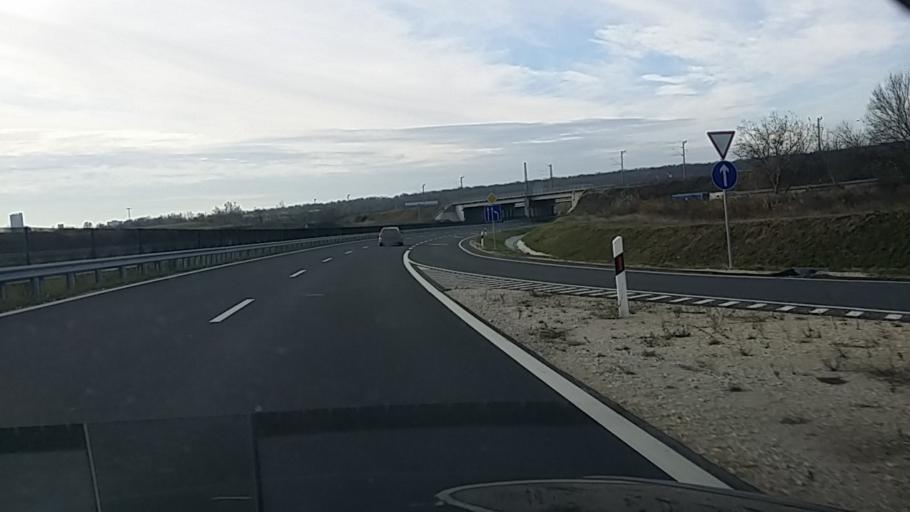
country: HU
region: Veszprem
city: Varpalota
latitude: 47.1851
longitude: 18.1360
